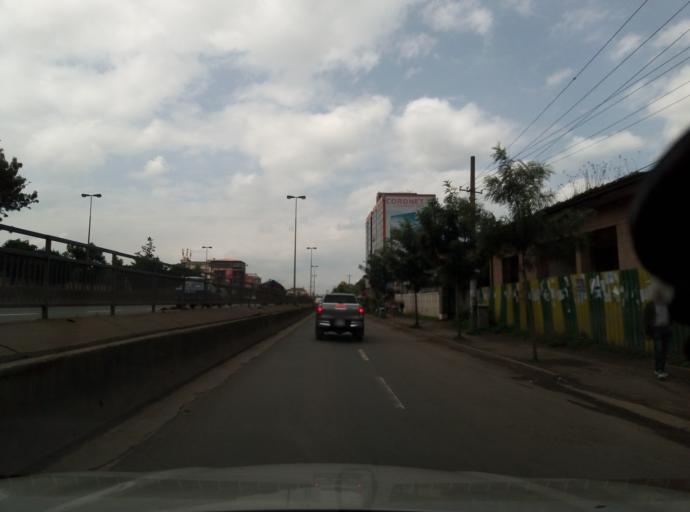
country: ET
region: Adis Abeba
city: Addis Ababa
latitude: 9.0030
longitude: 38.7188
